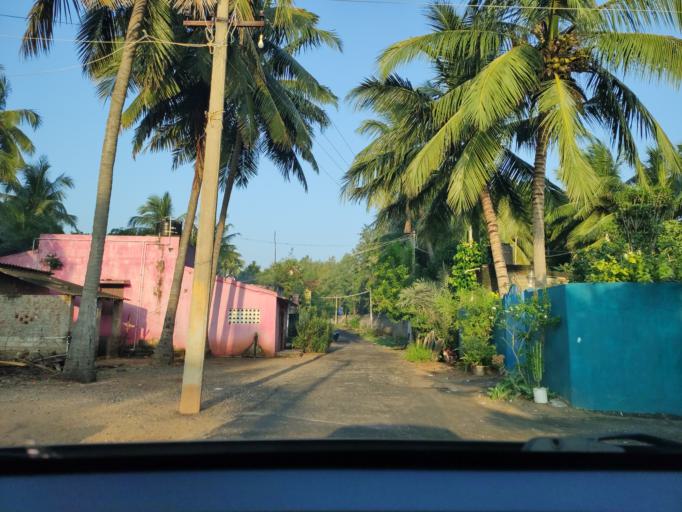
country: IN
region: Tamil Nadu
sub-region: Villupuram
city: Auroville
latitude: 12.0643
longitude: 79.8824
